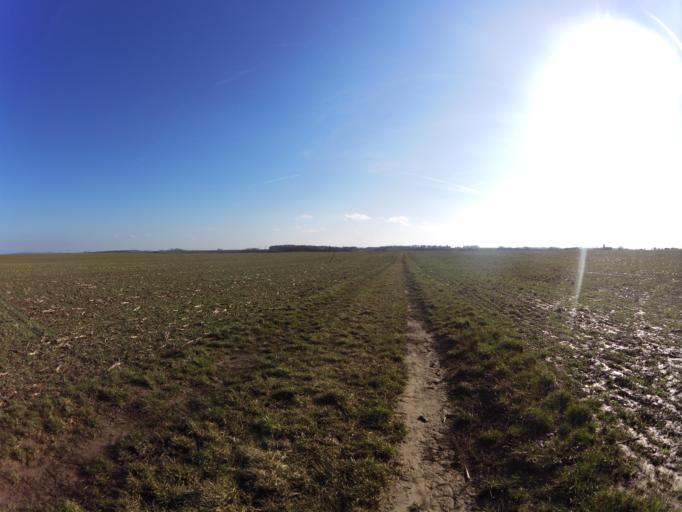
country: DE
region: Bavaria
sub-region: Regierungsbezirk Unterfranken
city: Giebelstadt
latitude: 49.6781
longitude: 9.9677
